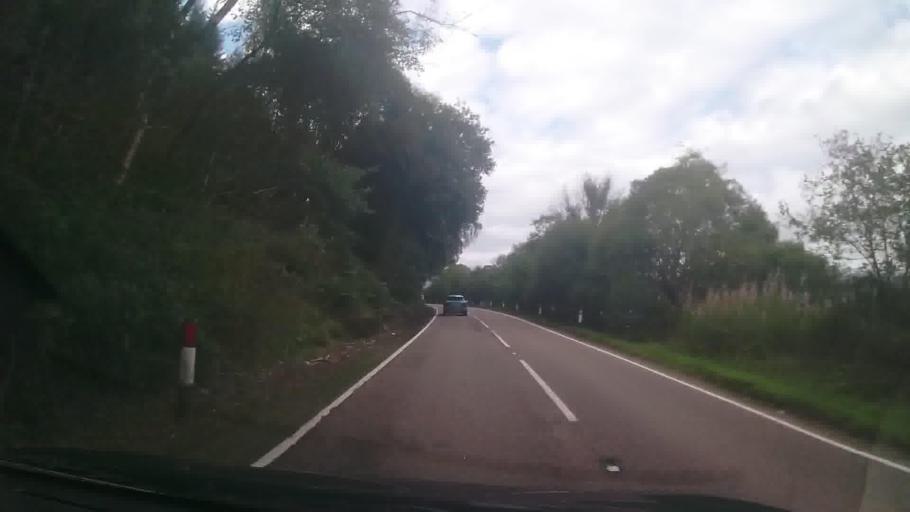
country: GB
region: Scotland
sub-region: Highland
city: Fort William
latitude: 56.6857
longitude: -5.2004
